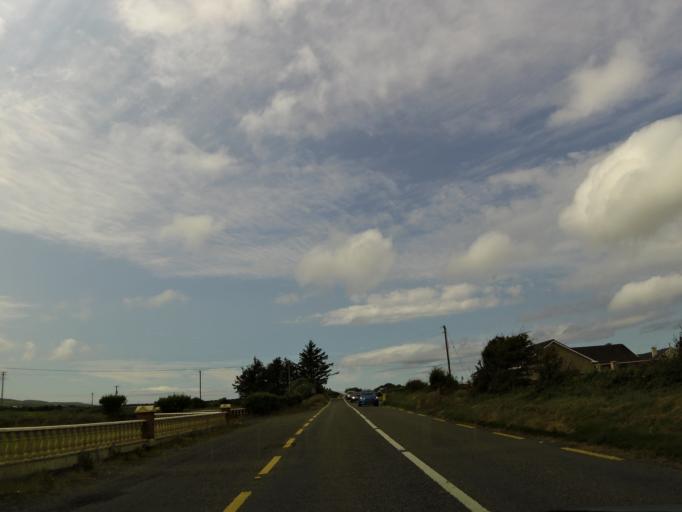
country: IE
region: Munster
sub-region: An Clar
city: Kilrush
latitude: 52.6744
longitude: -9.6098
